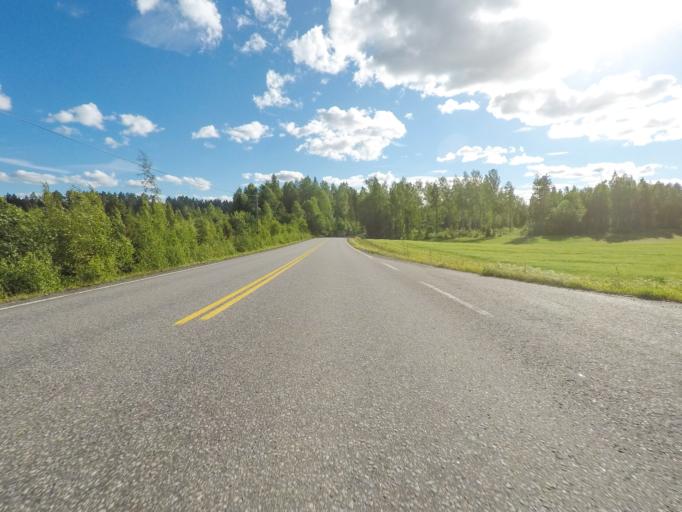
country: FI
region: Uusimaa
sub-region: Helsinki
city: Sammatti
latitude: 60.3351
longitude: 23.8973
